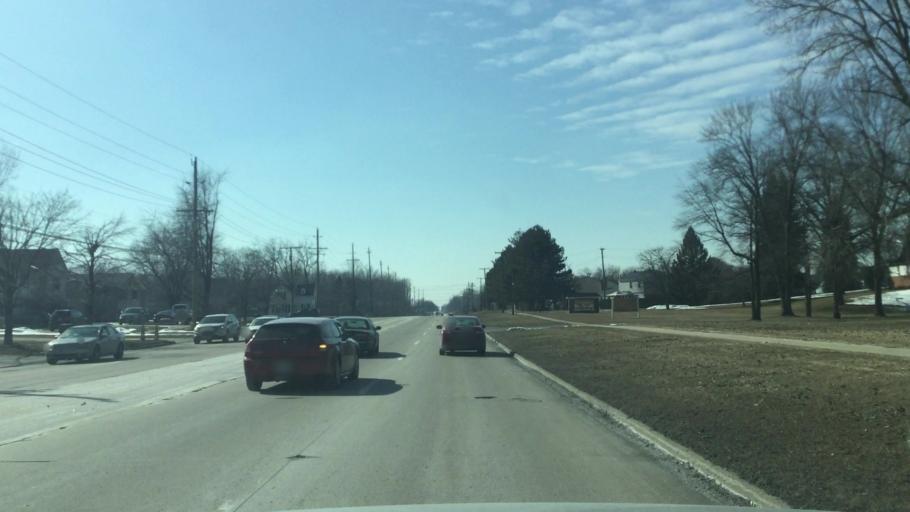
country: US
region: Michigan
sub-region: Wayne County
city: Westland
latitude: 42.3099
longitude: -83.3988
